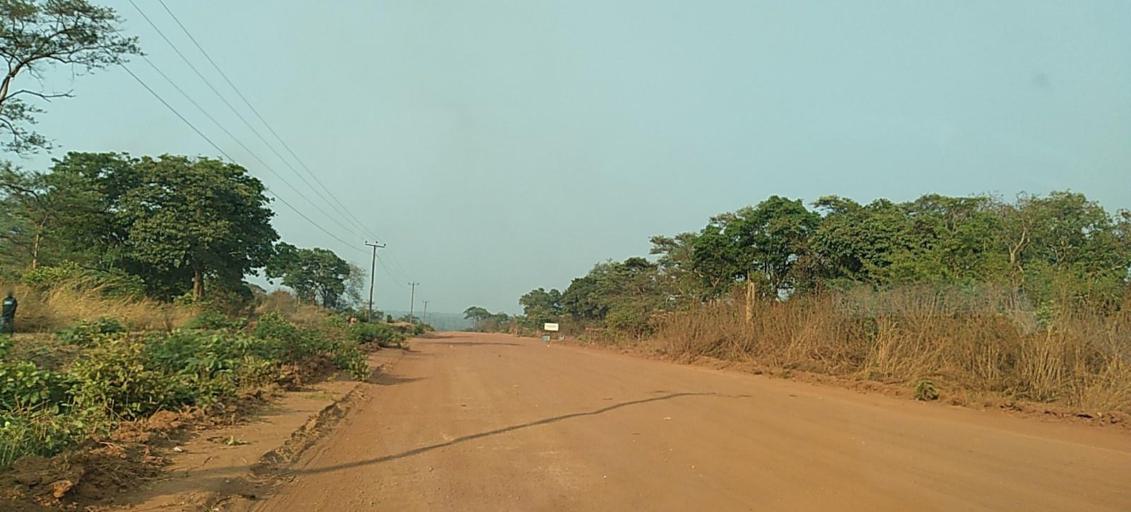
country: ZM
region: Copperbelt
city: Chingola
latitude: -12.8630
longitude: 27.6103
